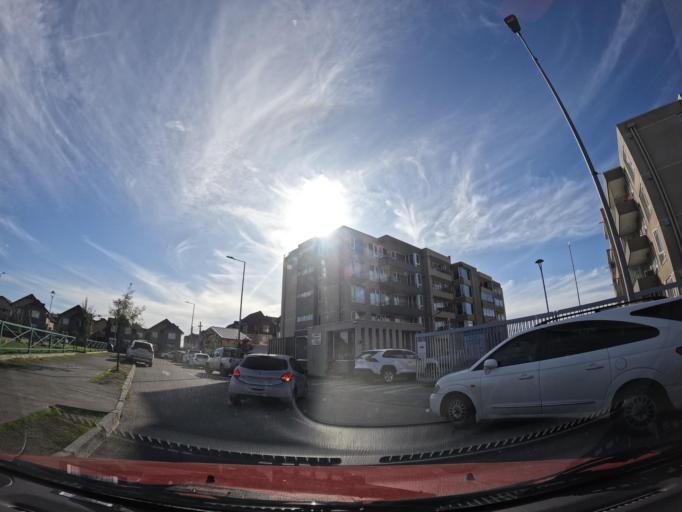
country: CL
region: Biobio
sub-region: Provincia de Concepcion
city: Concepcion
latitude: -36.7687
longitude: -73.0698
